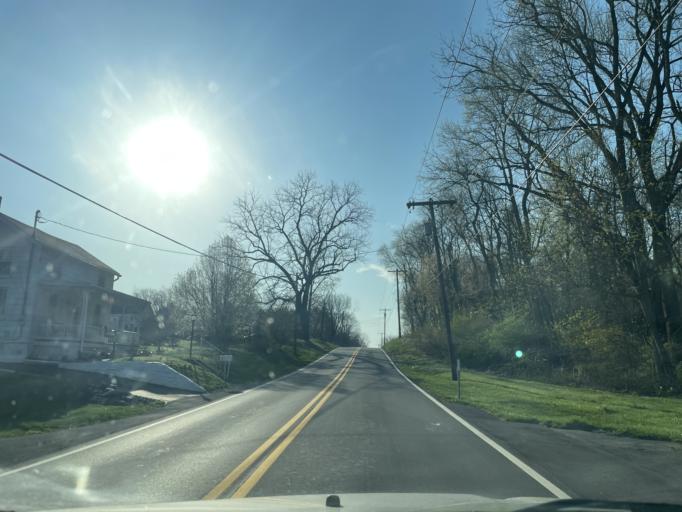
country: US
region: Maryland
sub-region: Washington County
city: Saint James
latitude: 39.5477
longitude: -77.7255
